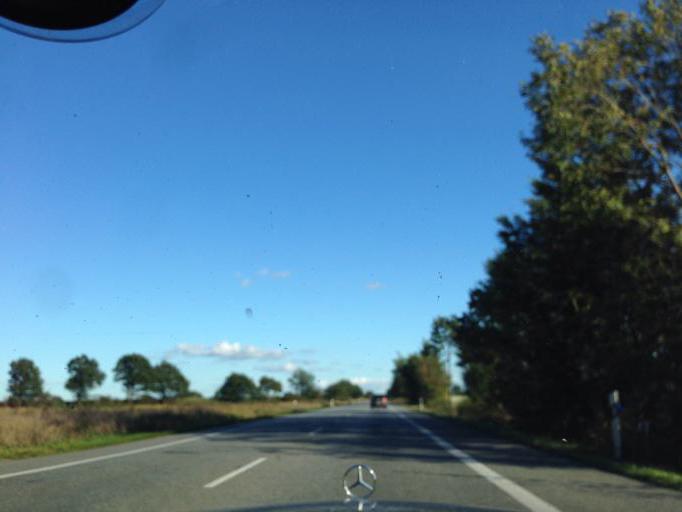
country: DE
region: Schleswig-Holstein
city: Wahlstedt
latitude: 53.9815
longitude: 10.2022
